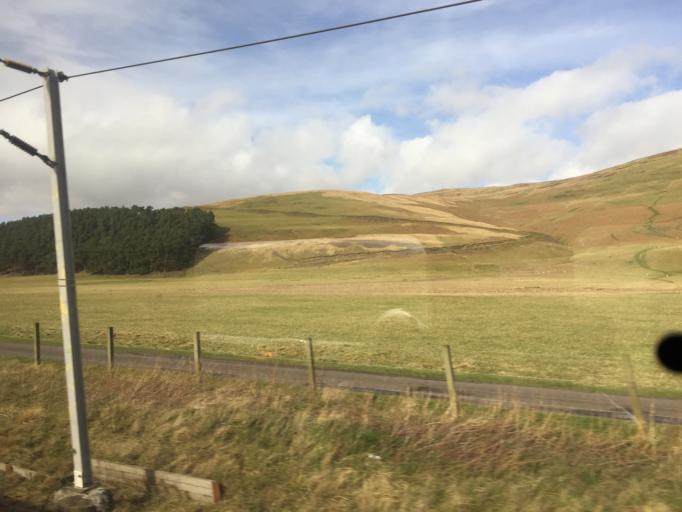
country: GB
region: Scotland
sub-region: South Lanarkshire
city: Douglas
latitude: 55.4726
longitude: -3.6714
